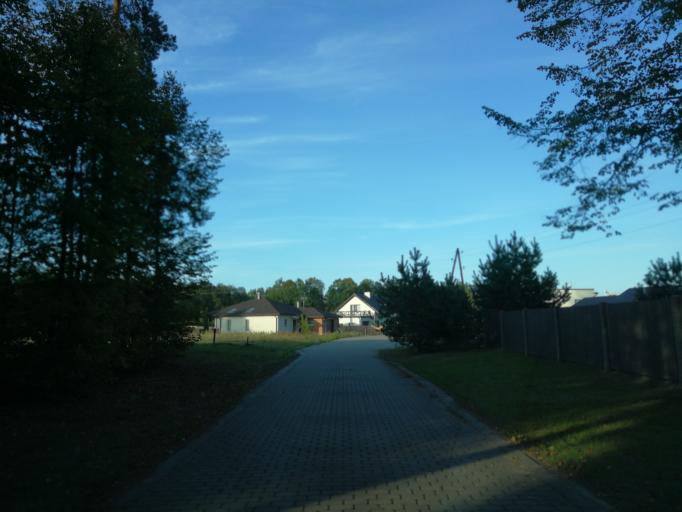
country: LV
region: Garkalne
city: Garkalne
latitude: 57.0861
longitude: 24.4748
